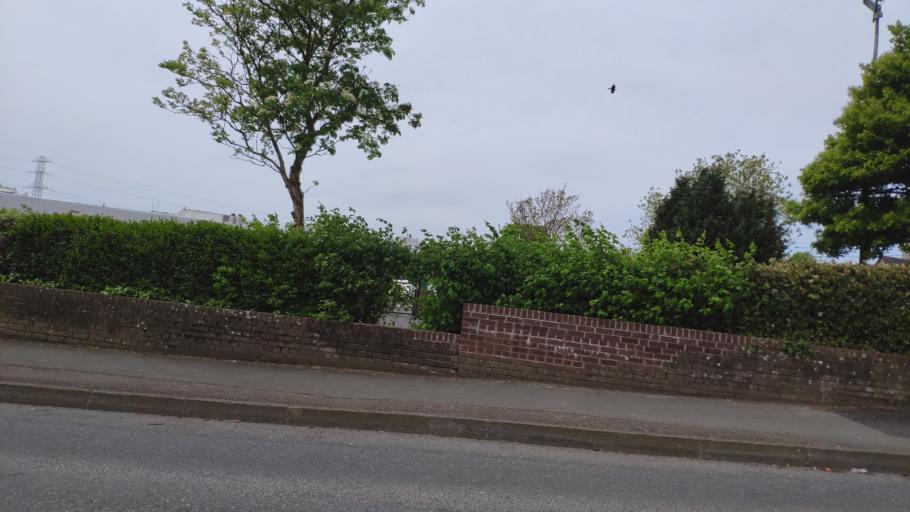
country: IE
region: Munster
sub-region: County Cork
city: Cork
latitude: 51.9168
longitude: -8.4467
